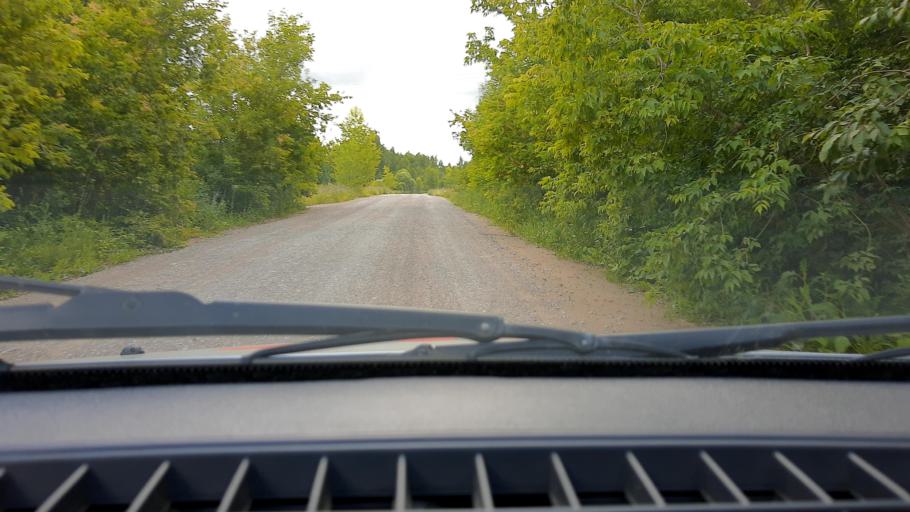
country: RU
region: Bashkortostan
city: Ufa
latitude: 54.6695
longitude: 56.0705
